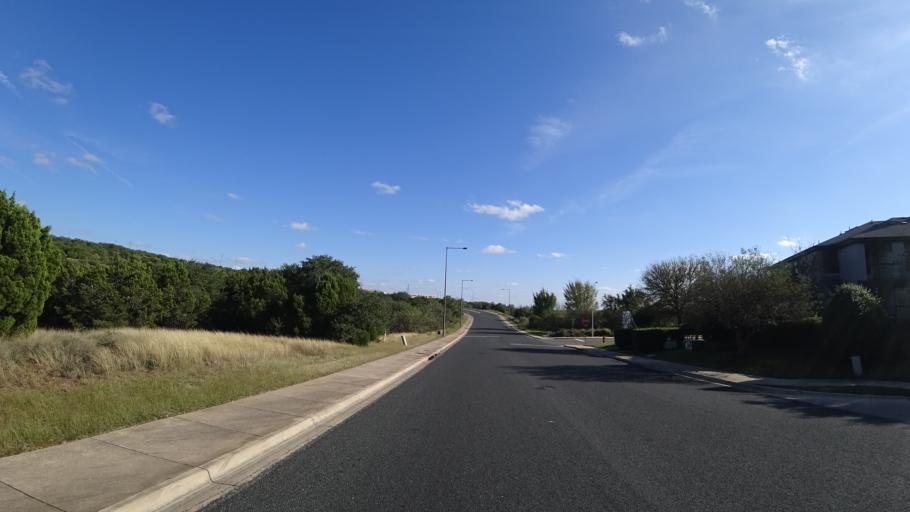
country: US
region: Texas
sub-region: Travis County
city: Barton Creek
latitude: 30.2514
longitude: -97.8690
